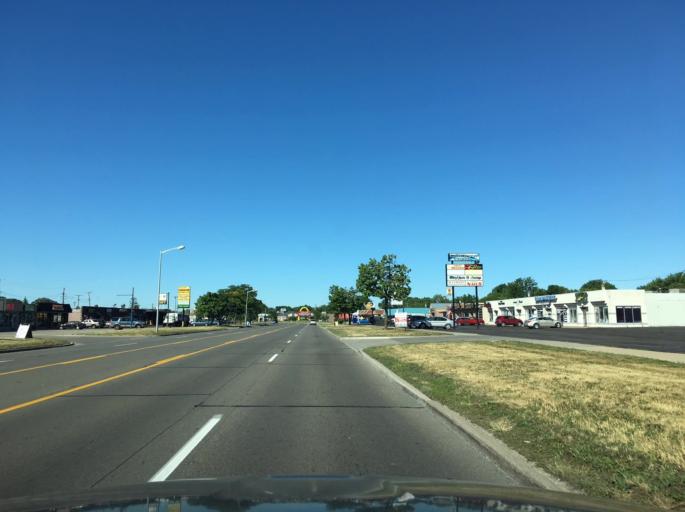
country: US
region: Michigan
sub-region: Macomb County
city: Saint Clair Shores
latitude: 42.5273
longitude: -82.8935
